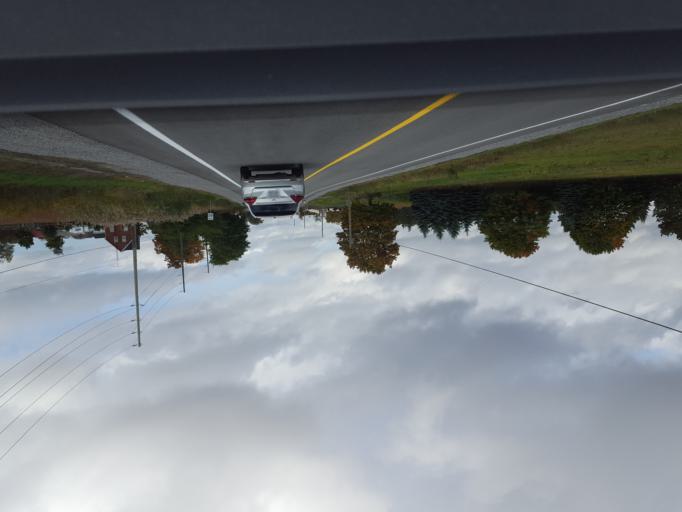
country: CA
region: Ontario
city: Pickering
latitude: 43.8520
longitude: -79.1850
